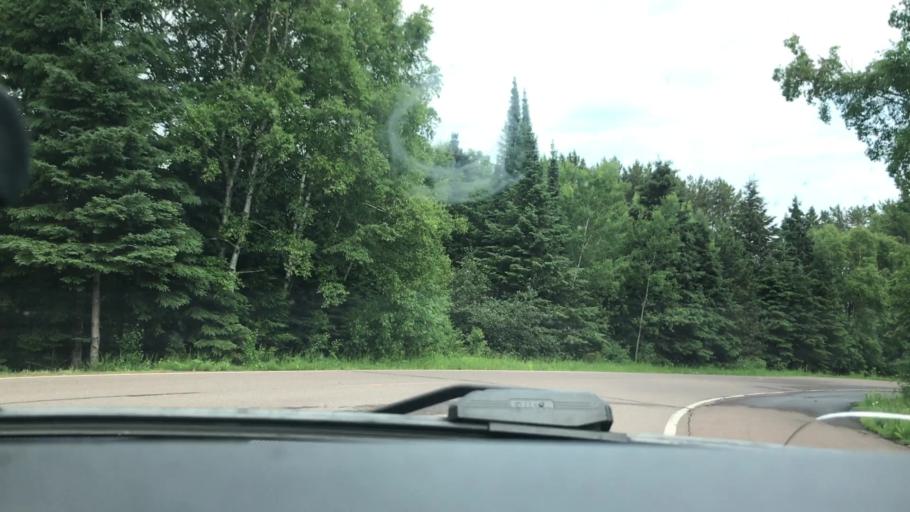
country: CA
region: Ontario
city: Neebing
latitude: 47.9645
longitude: -89.6855
